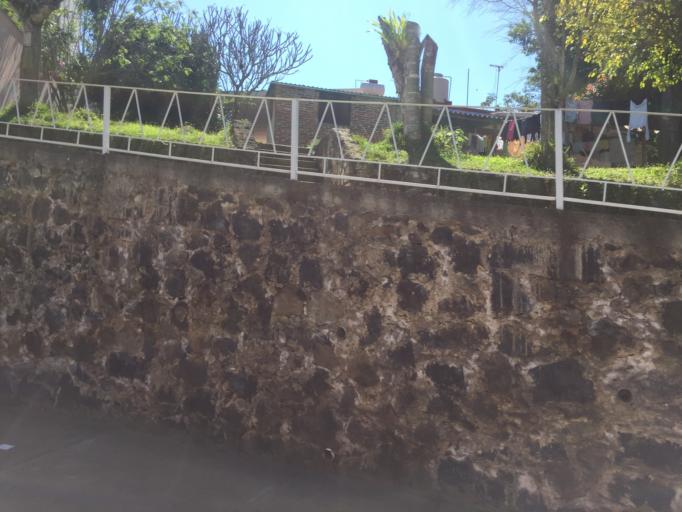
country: MX
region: Veracruz
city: El Castillo
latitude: 19.5309
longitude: -96.8832
